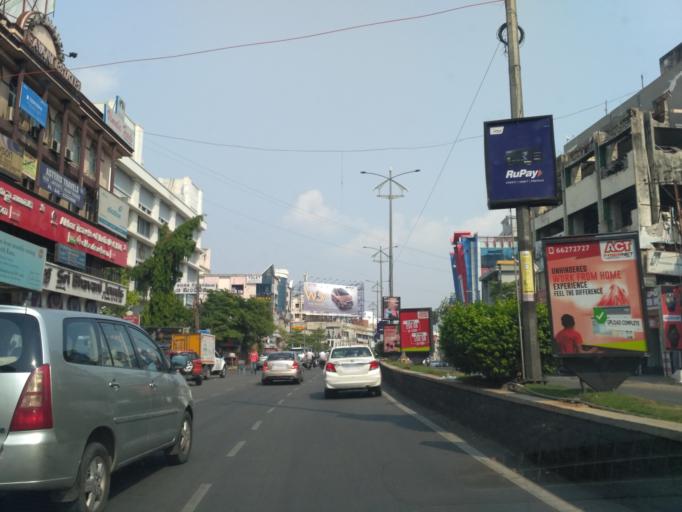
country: IN
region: Telangana
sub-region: Hyderabad
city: Hyderabad
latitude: 17.4064
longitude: 78.4781
